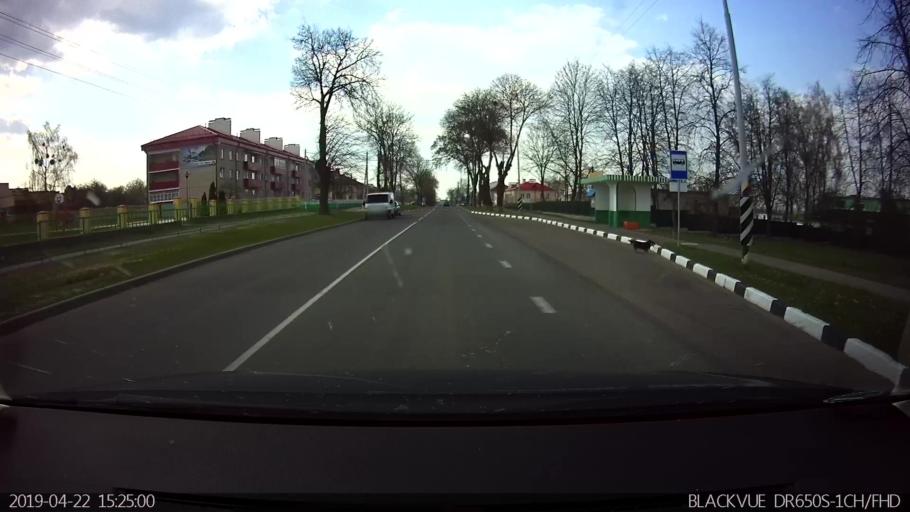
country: BY
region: Brest
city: Vysokaye
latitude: 52.3630
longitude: 23.4006
